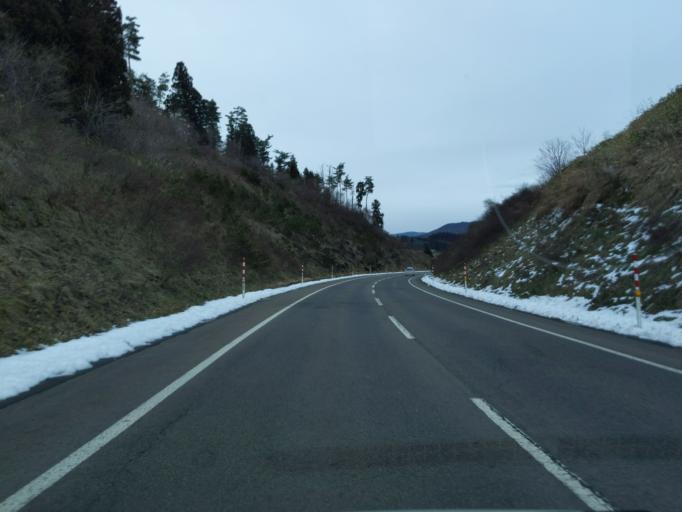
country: JP
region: Iwate
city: Mizusawa
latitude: 39.1683
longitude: 141.2508
